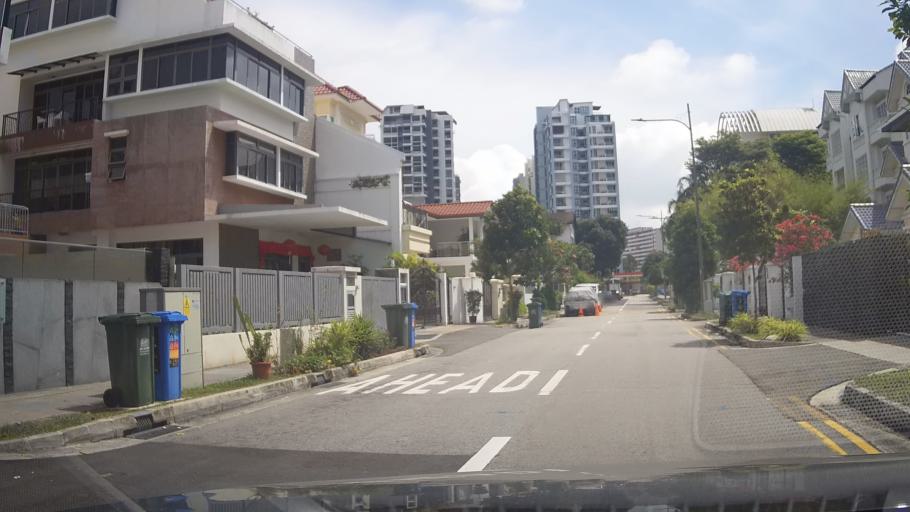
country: SG
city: Singapore
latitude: 1.3112
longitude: 103.8926
